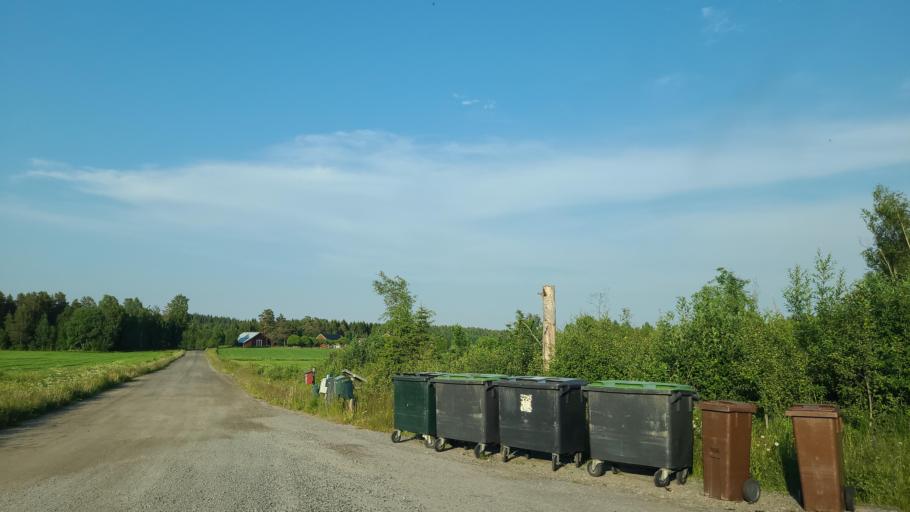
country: SE
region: Vaesterbotten
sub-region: Skelleftea Kommun
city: Burea
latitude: 64.3434
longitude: 21.3441
